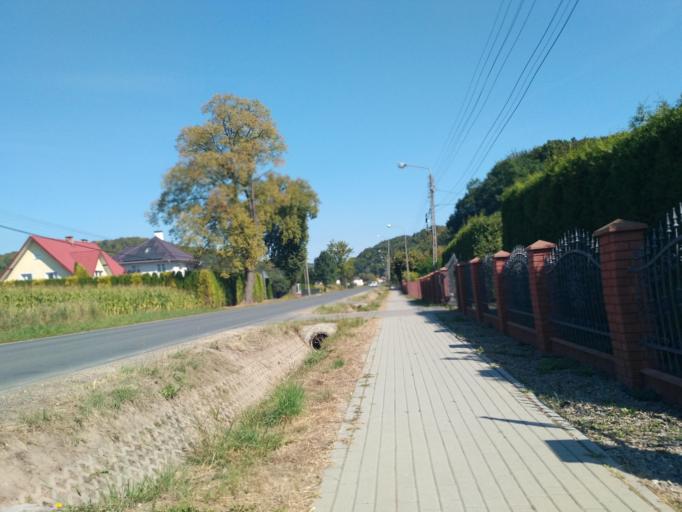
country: PL
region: Subcarpathian Voivodeship
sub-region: Powiat brzozowski
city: Grabownica Starzenska
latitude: 49.6622
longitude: 22.0805
